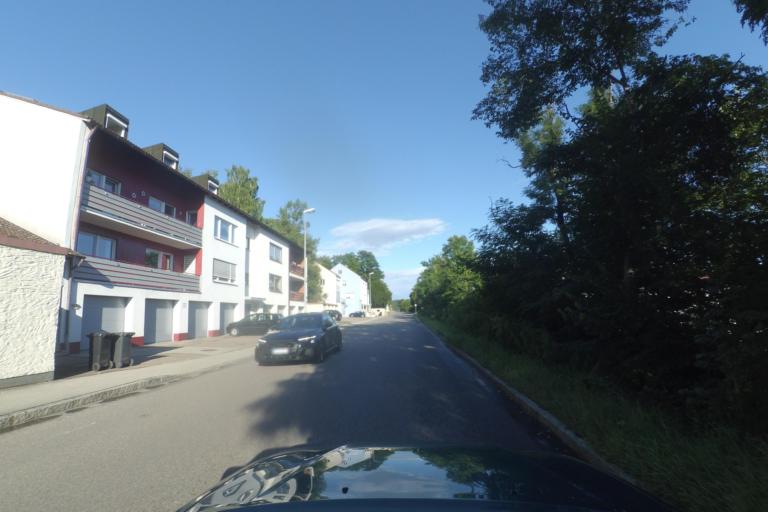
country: DE
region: Bavaria
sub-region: Upper Bavaria
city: Eichstaett
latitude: 48.8835
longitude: 11.2100
